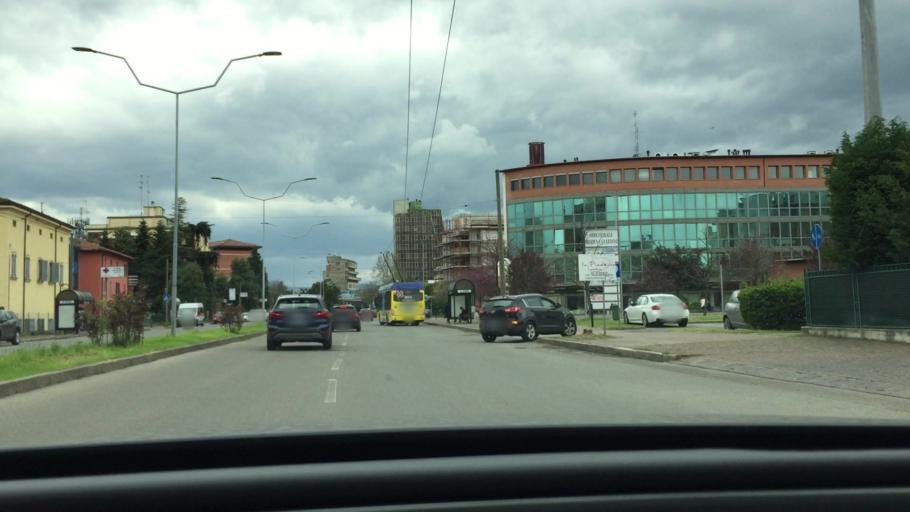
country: IT
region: Emilia-Romagna
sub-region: Provincia di Modena
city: Modena
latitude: 44.6383
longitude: 10.9059
